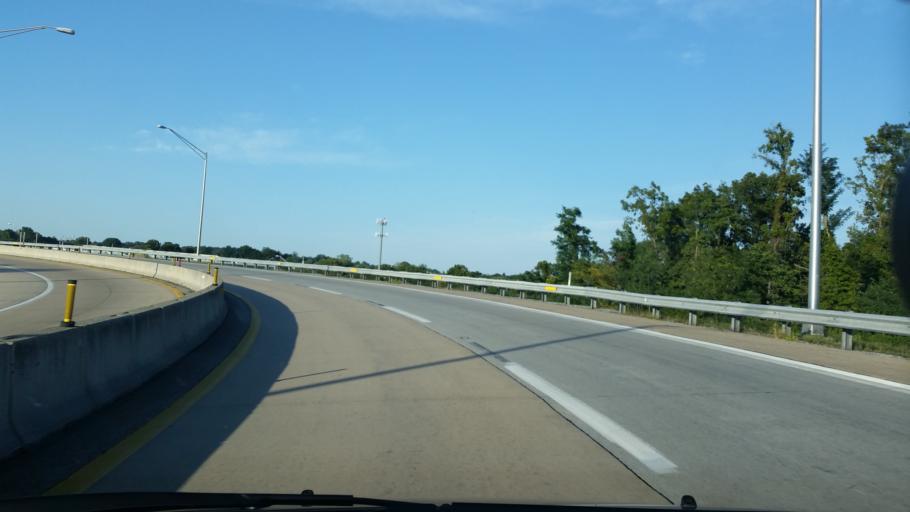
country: US
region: Pennsylvania
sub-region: Dauphin County
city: Highspire
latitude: 40.2136
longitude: -76.7862
